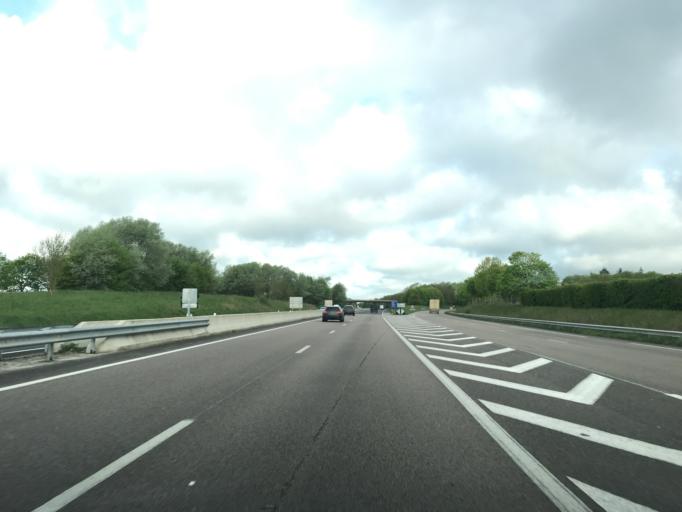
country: FR
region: Haute-Normandie
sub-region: Departement de l'Eure
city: Corneville-sur-Risle
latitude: 49.3804
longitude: 0.6121
